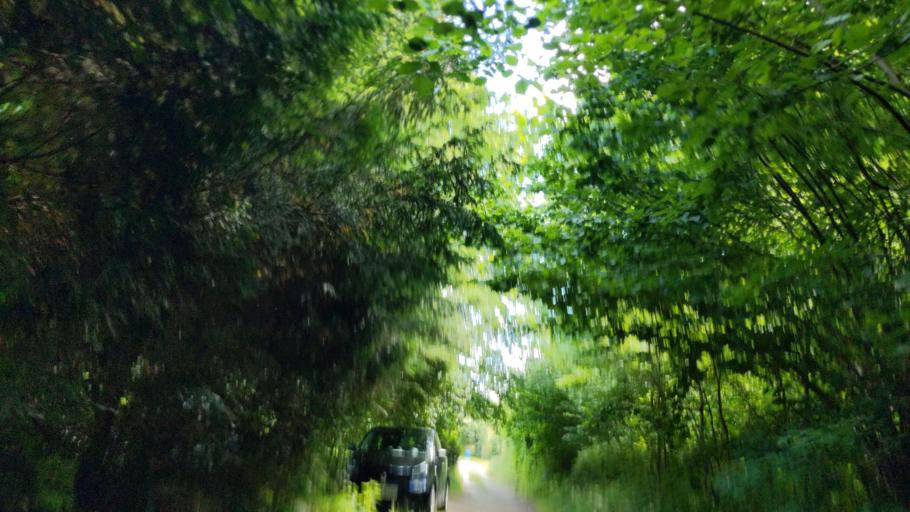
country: DE
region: Schleswig-Holstein
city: Buchholz
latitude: 53.7352
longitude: 10.7468
